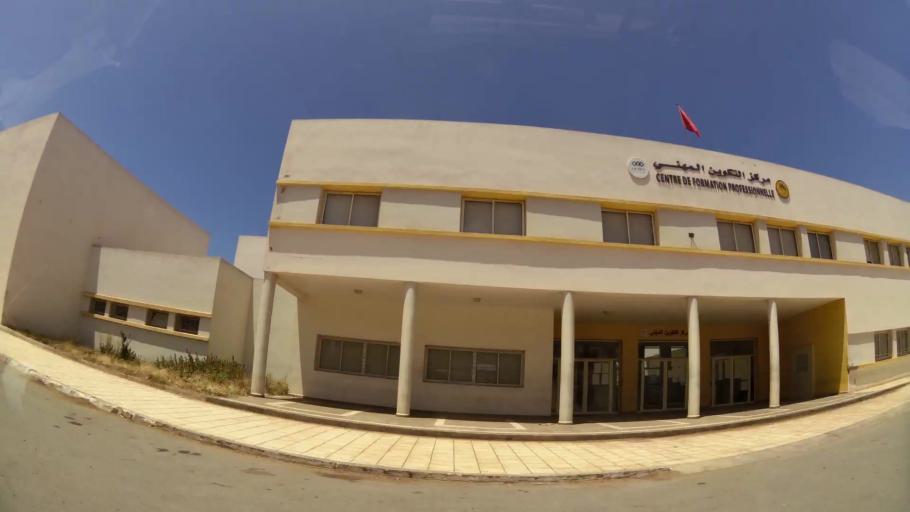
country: MA
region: Gharb-Chrarda-Beni Hssen
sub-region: Kenitra Province
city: Kenitra
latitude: 34.2510
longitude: -6.6257
